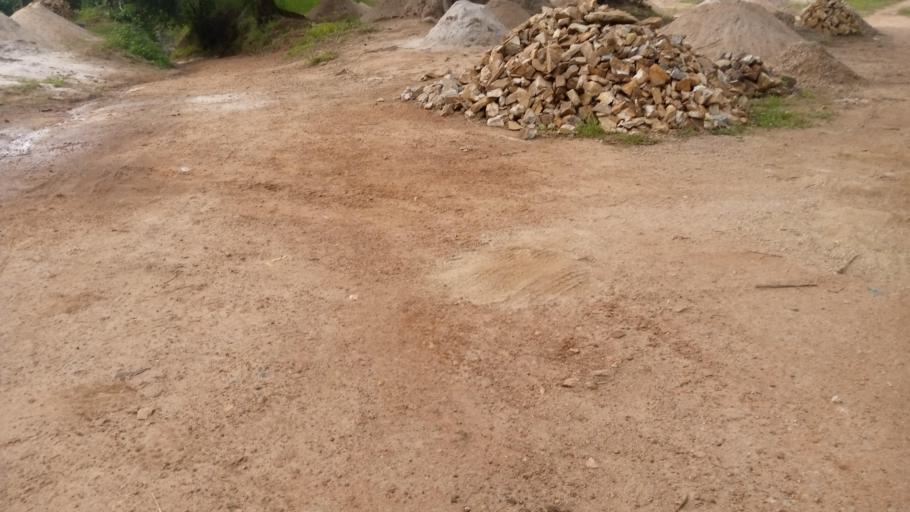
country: SL
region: Southern Province
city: Pujehun
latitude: 7.3468
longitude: -11.7178
